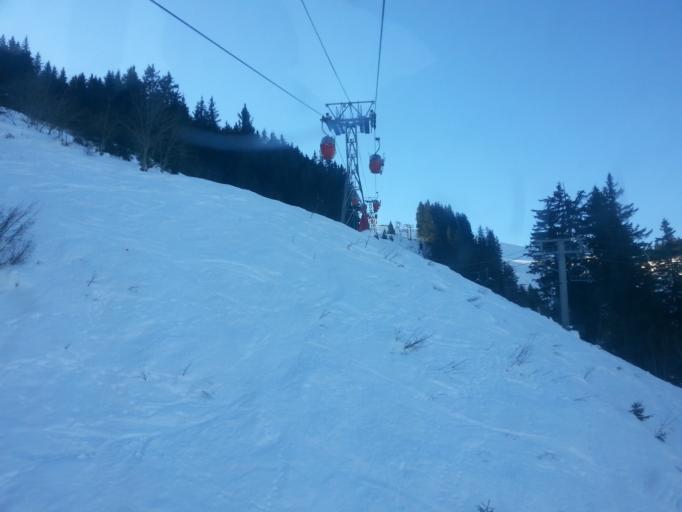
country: FR
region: Rhone-Alpes
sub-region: Departement de la Haute-Savoie
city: Samoens
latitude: 46.0591
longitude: 6.6993
